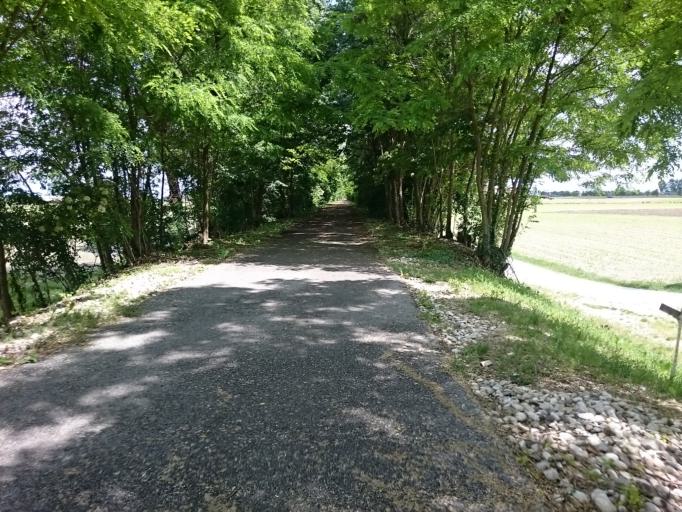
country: IT
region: Veneto
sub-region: Provincia di Padova
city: Campodoro
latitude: 45.4980
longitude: 11.7394
